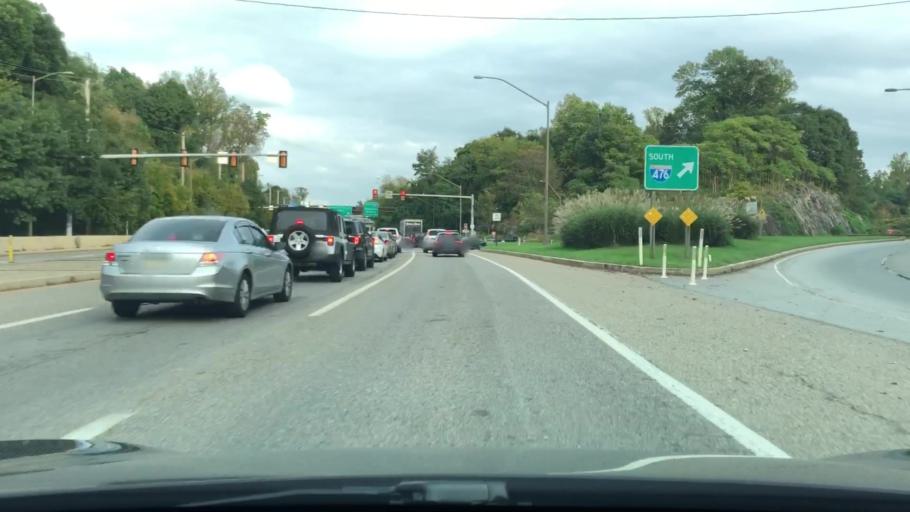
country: US
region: Pennsylvania
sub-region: Delaware County
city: Radnor
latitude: 40.0376
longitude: -75.3605
